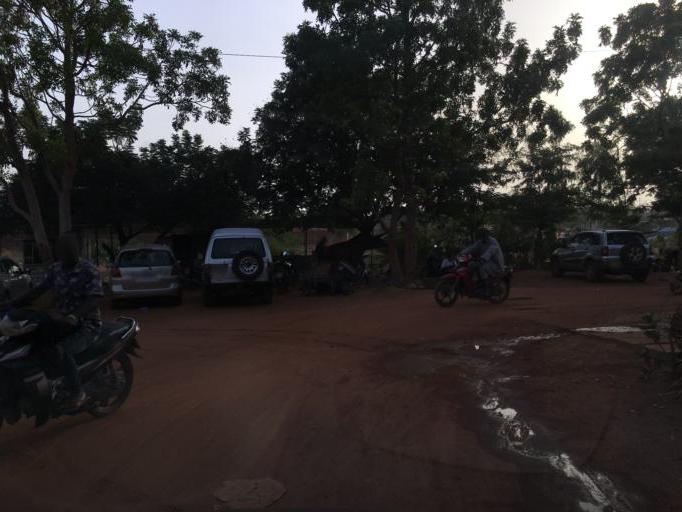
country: BF
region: Centre
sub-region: Kadiogo Province
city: Ouagadougou
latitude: 12.3602
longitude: -1.4990
